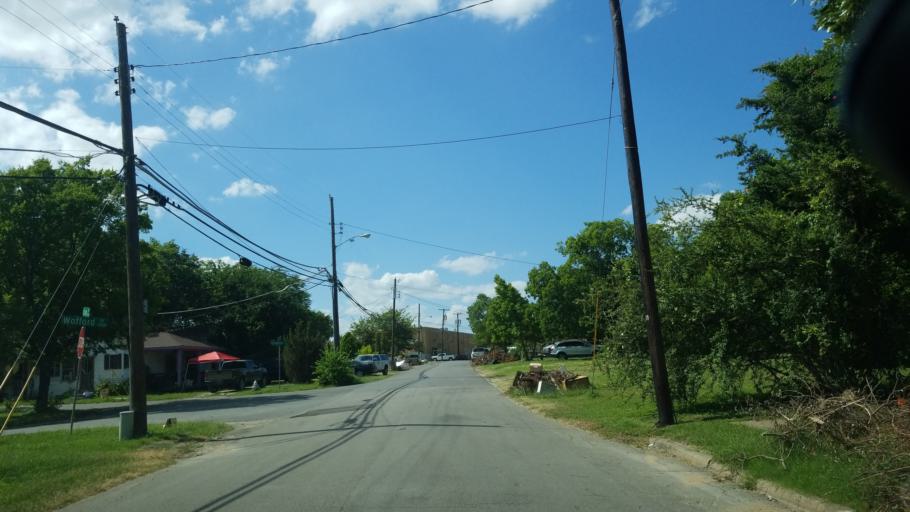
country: US
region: Texas
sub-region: Dallas County
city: Balch Springs
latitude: 32.7700
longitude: -96.6959
